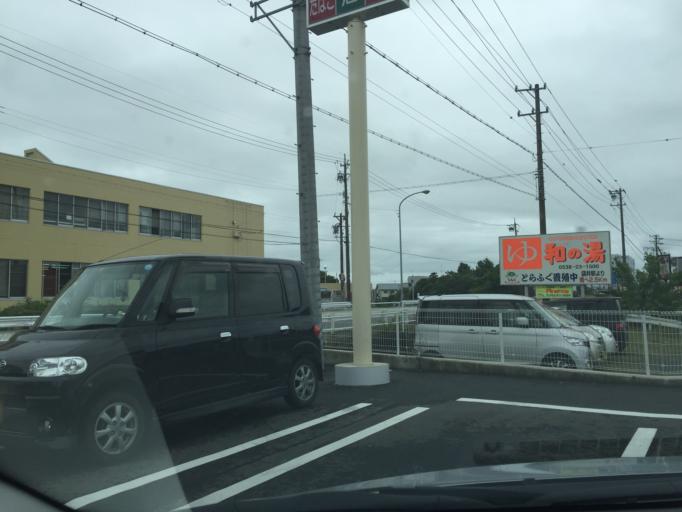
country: JP
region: Shizuoka
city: Fukuroi
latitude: 34.7514
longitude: 137.9245
